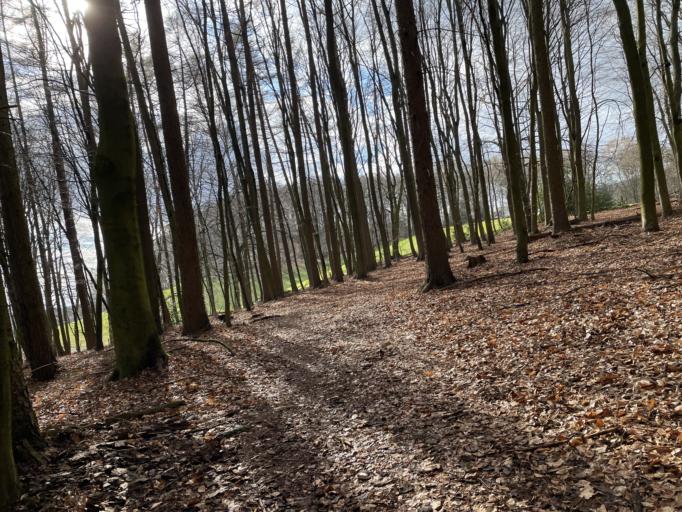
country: DE
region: North Rhine-Westphalia
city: Porta Westfalica
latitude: 52.2345
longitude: 8.9582
